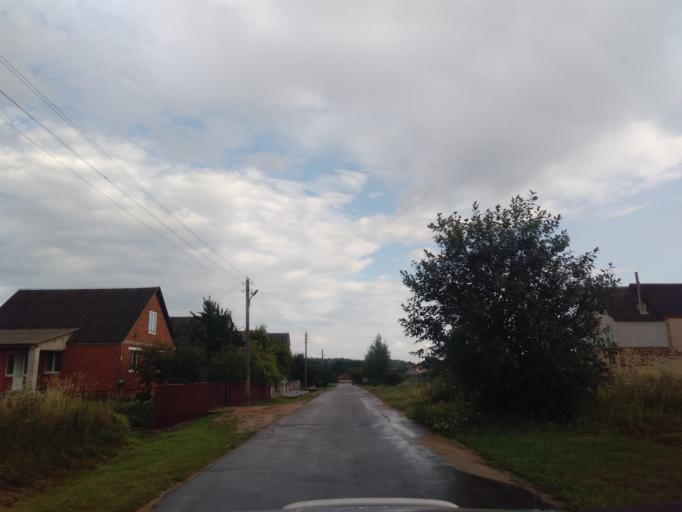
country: BY
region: Minsk
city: Kapyl'
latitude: 53.1650
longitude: 27.0874
